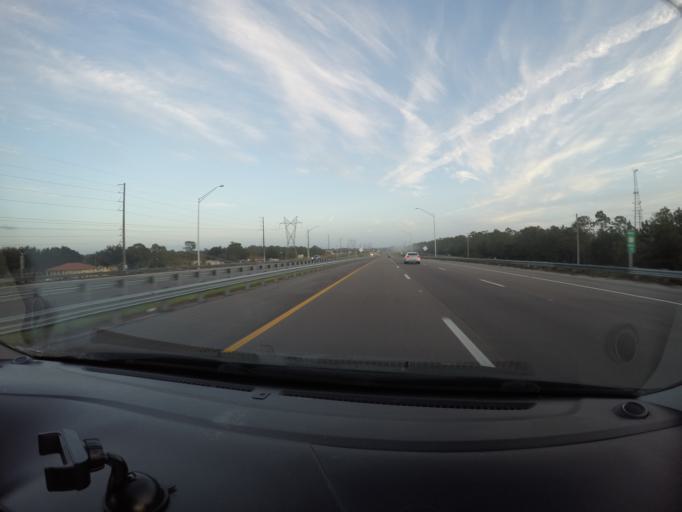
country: US
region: Florida
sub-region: Orange County
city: Azalea Park
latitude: 28.5259
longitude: -81.2508
